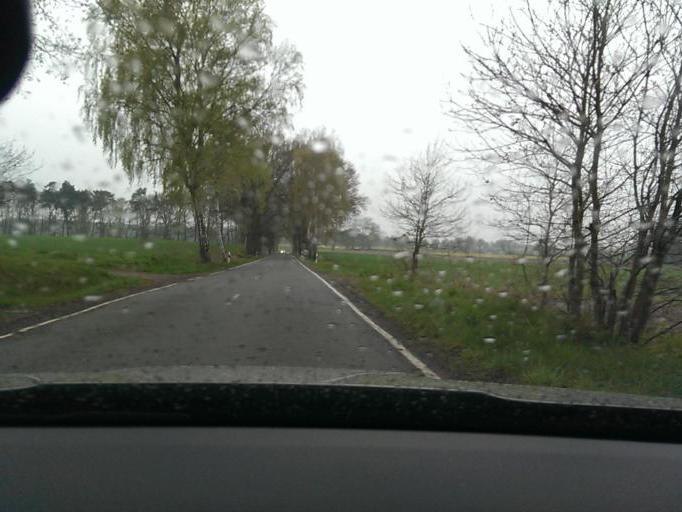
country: DE
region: Lower Saxony
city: Steimbke
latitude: 52.6059
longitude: 9.4713
